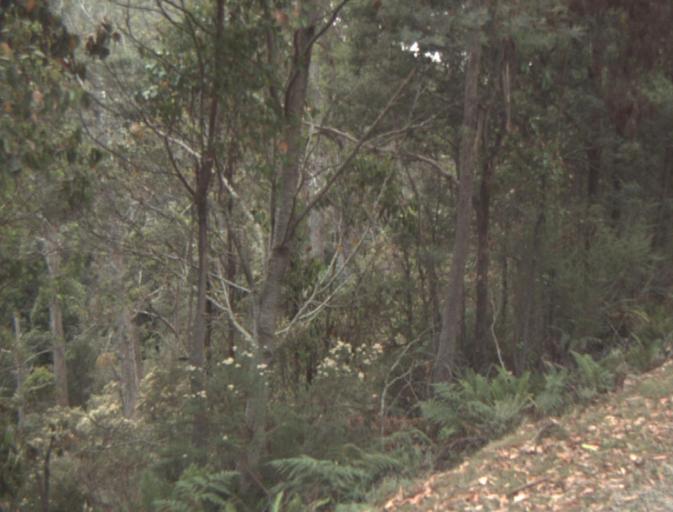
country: AU
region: Tasmania
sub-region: Dorset
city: Scottsdale
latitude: -41.3908
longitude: 147.5098
